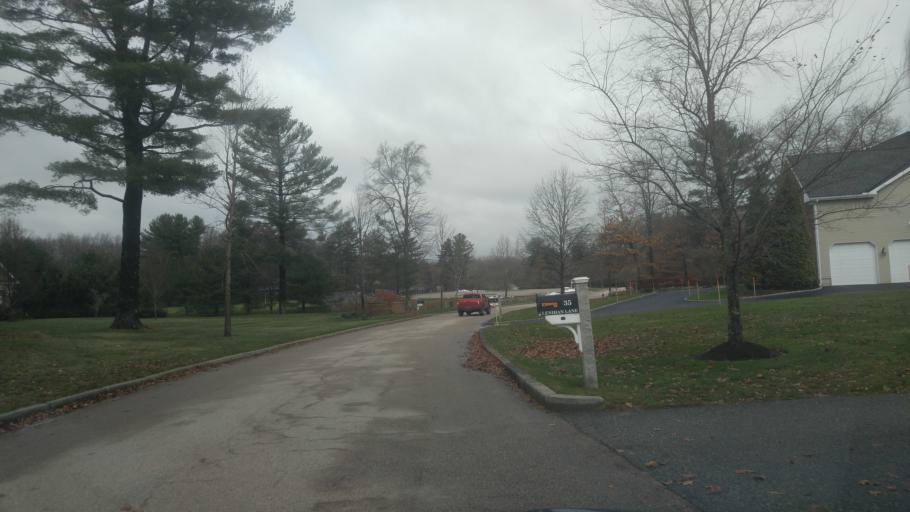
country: US
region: Rhode Island
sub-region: Kent County
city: West Warwick
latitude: 41.6394
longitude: -71.5347
